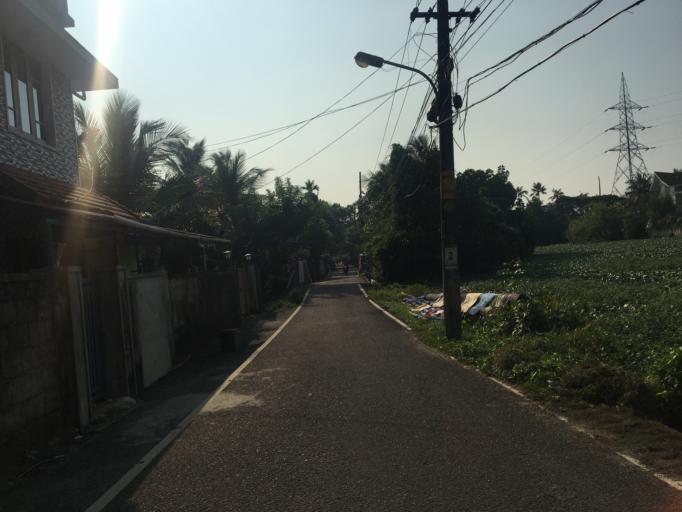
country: IN
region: Kerala
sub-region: Ernakulam
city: Cochin
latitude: 9.9505
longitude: 76.3090
